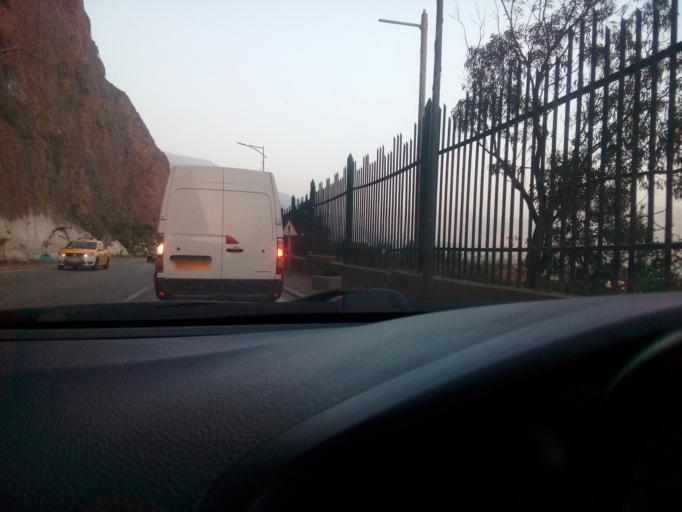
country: DZ
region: Oran
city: Mers el Kebir
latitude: 35.7119
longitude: -0.6805
